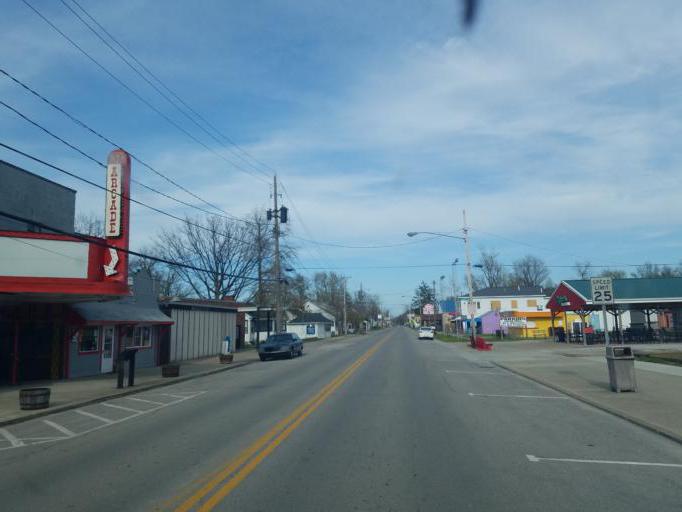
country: US
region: Ohio
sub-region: Ashtabula County
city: Geneva-on-the-Lake
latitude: 41.8609
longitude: -80.9474
